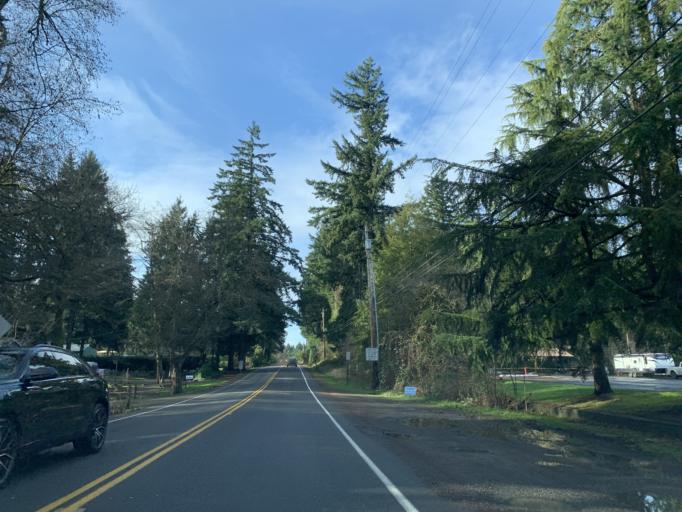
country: US
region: Washington
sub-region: King County
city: Lakeland South
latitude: 47.2885
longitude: -122.2937
